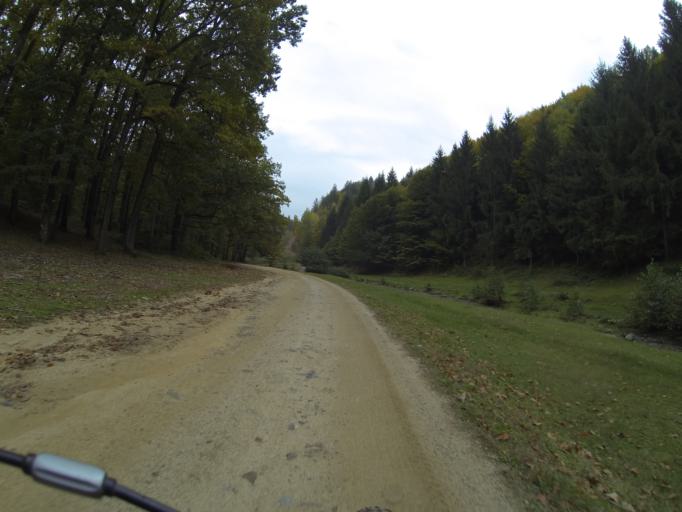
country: RO
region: Gorj
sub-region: Comuna Tismana
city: Sohodol
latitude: 45.0631
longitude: 22.8937
